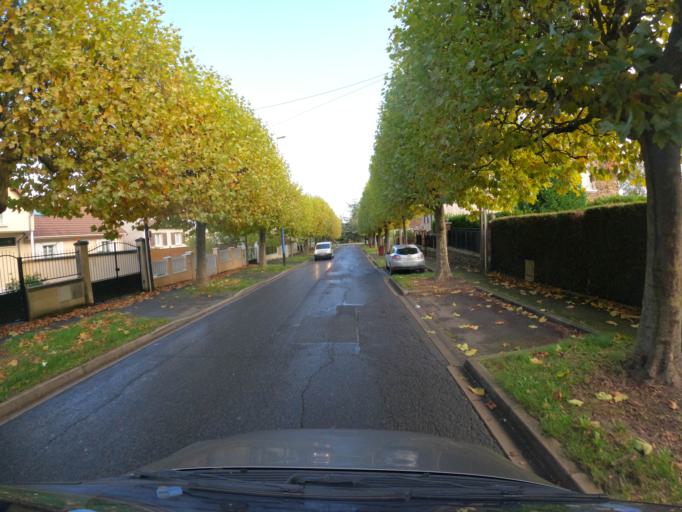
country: FR
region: Ile-de-France
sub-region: Departement de Seine-et-Marne
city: Brou-sur-Chantereine
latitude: 48.8954
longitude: 2.6193
